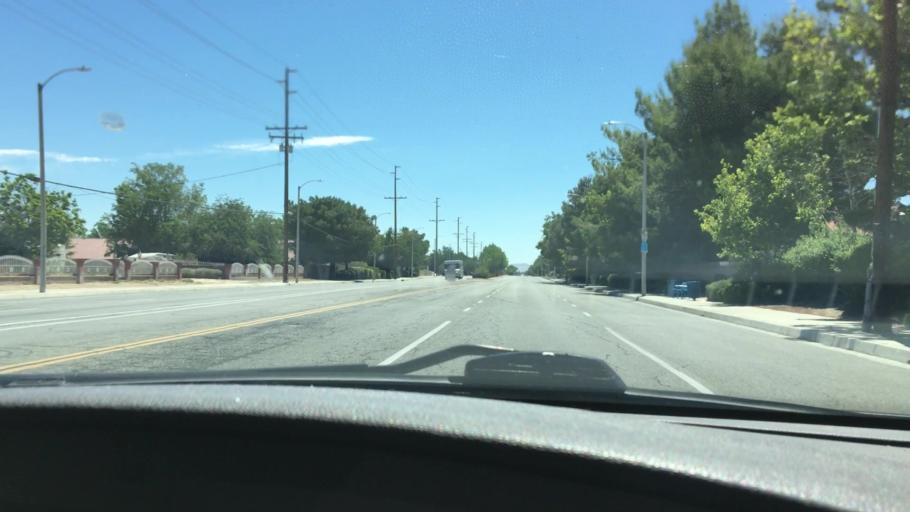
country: US
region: California
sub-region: Los Angeles County
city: Lancaster
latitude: 34.6750
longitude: -118.1033
